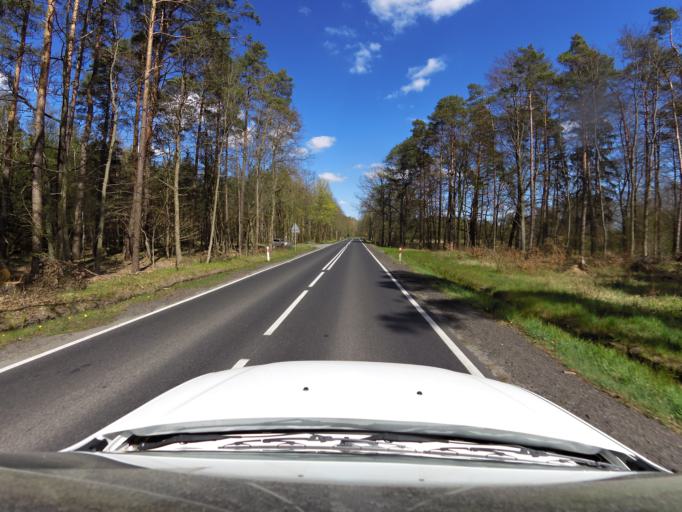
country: PL
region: West Pomeranian Voivodeship
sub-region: Powiat mysliborski
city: Debno
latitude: 52.7760
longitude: 14.7494
